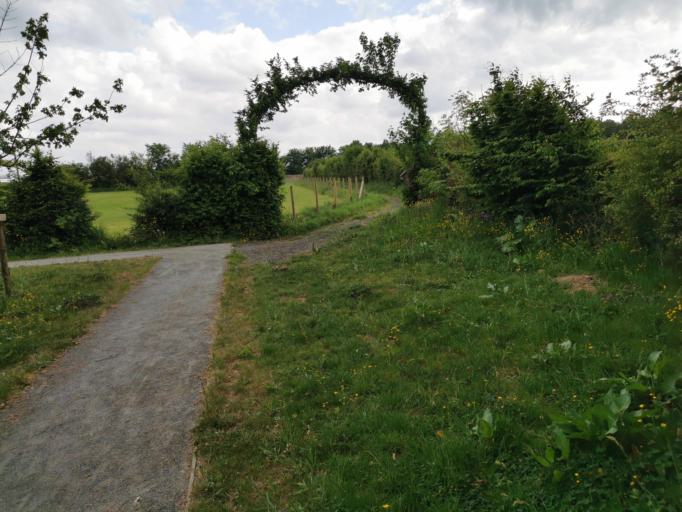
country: FR
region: Nord-Pas-de-Calais
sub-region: Departement du Nord
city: Anor
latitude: 49.9866
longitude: 4.0890
